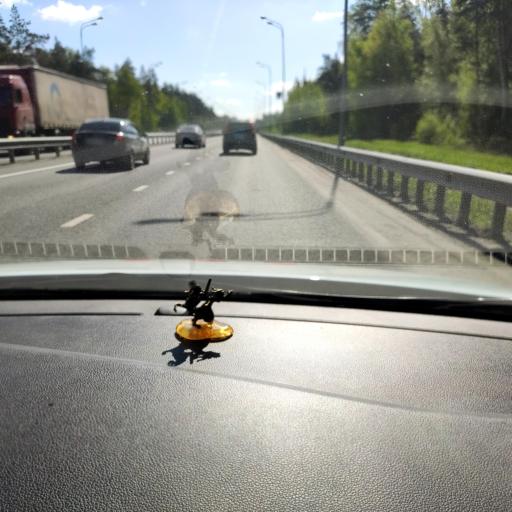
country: RU
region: Tatarstan
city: Staroye Arakchino
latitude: 55.8309
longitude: 49.0023
